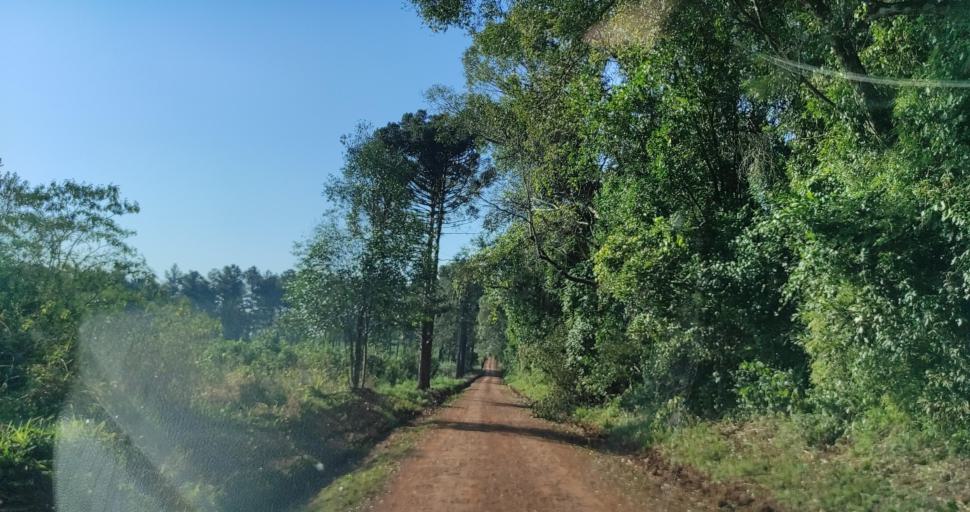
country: AR
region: Misiones
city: Capiovi
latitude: -26.8791
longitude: -55.1077
